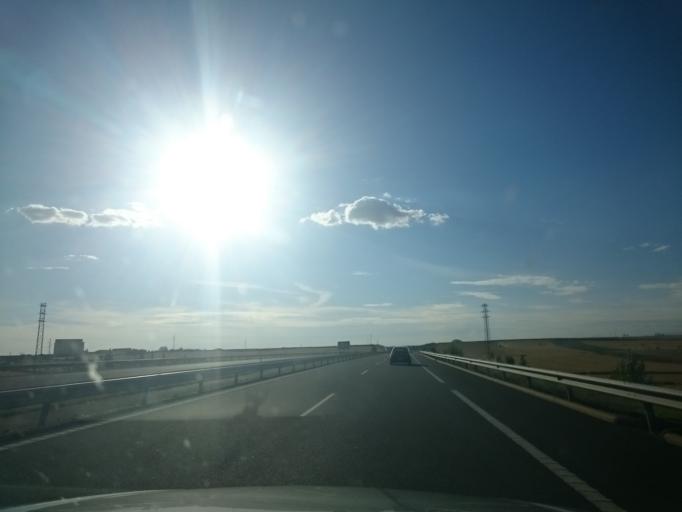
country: ES
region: Castille and Leon
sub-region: Provincia de Burgos
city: Melgar de Fernamental
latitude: 42.4057
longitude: -4.2293
